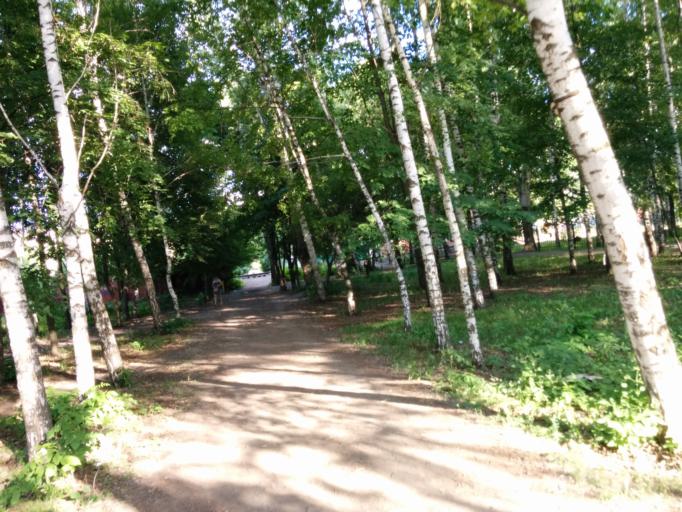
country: RU
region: Tambov
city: Tambov
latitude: 52.7472
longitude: 41.4414
